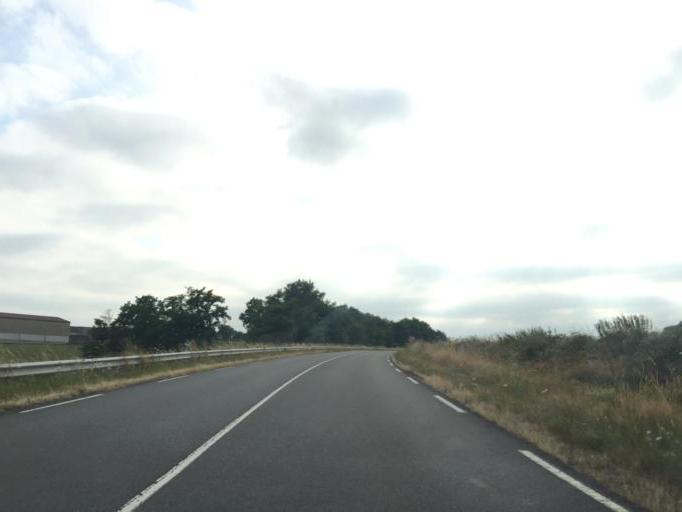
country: FR
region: Auvergne
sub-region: Departement de l'Allier
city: Molinet
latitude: 46.4538
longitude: 3.9227
